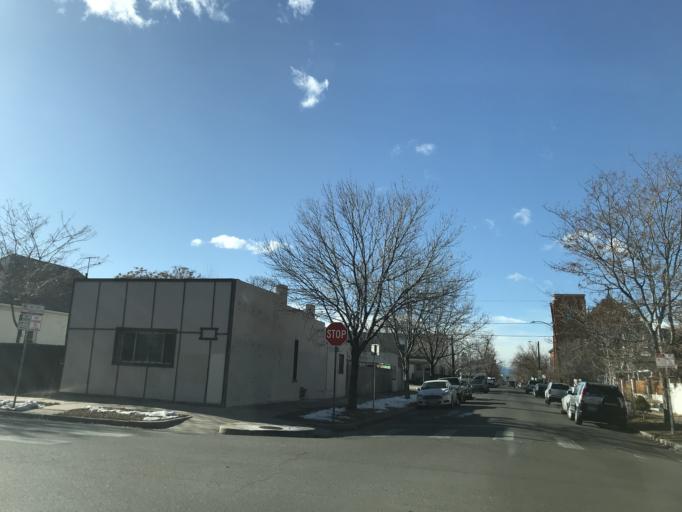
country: US
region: Colorado
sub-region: Denver County
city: Denver
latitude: 39.7670
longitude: -104.9681
